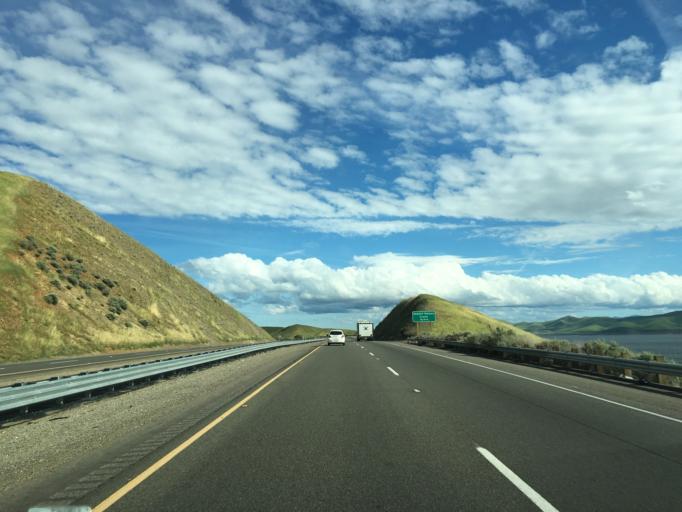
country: US
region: California
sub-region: Merced County
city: Gustine
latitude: 37.0882
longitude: -121.1140
